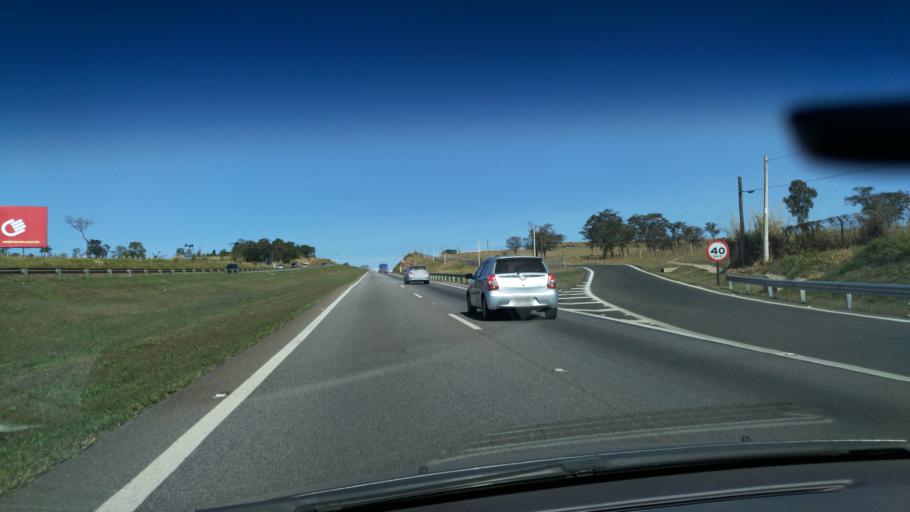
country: BR
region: Sao Paulo
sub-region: Jaguariuna
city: Jaguariuna
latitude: -22.6664
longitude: -47.0030
